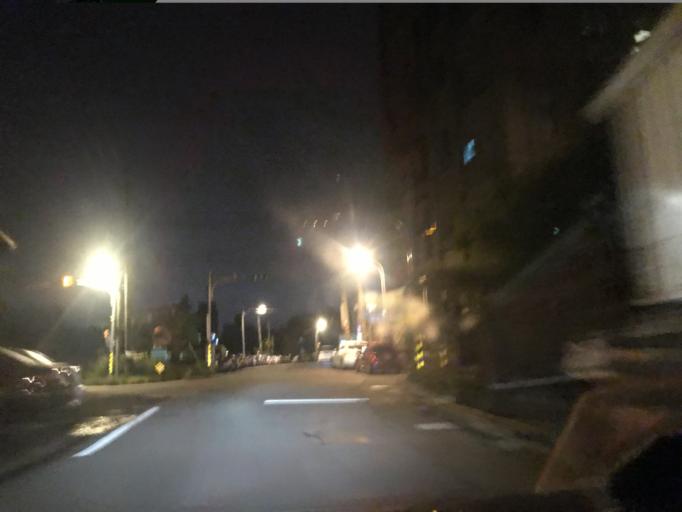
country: TW
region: Taiwan
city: Daxi
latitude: 24.8483
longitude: 121.2238
